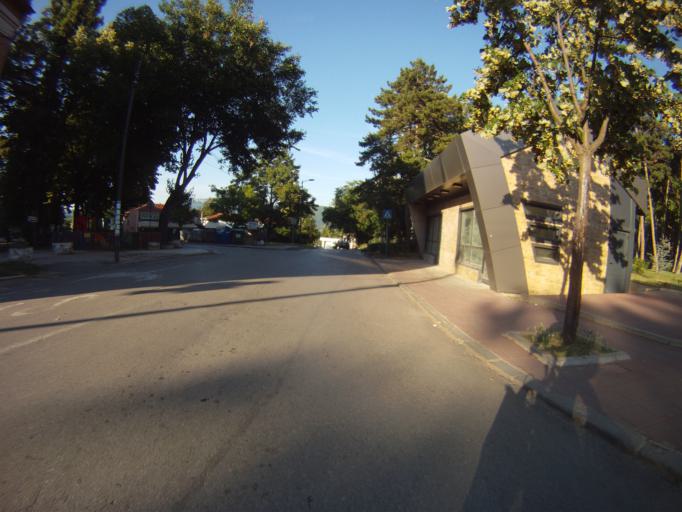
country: RS
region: Central Serbia
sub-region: Nisavski Okrug
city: Niska Banja
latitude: 43.2935
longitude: 22.0052
